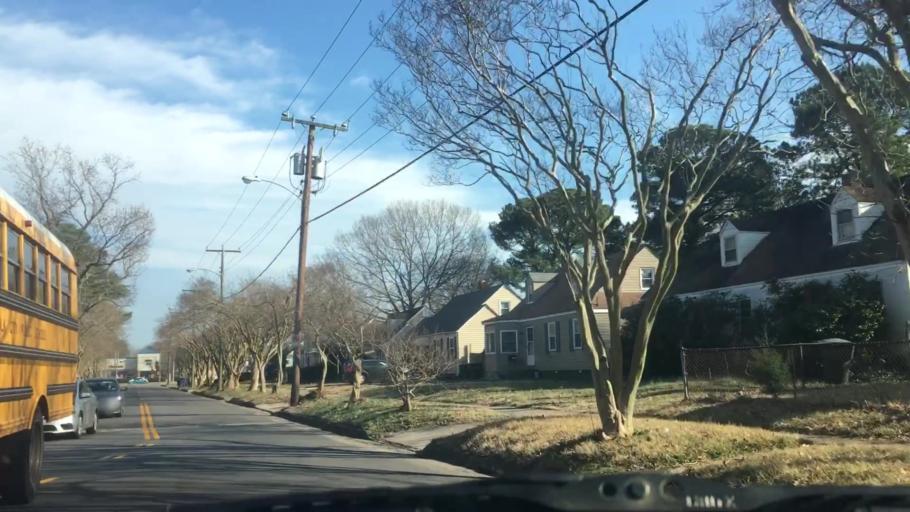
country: US
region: Virginia
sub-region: City of Norfolk
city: Norfolk
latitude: 36.8869
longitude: -76.2630
